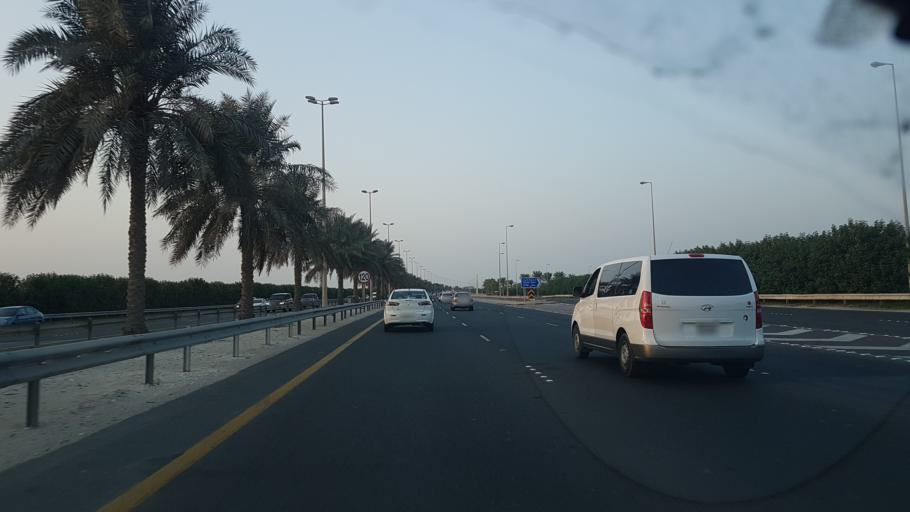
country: BH
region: Northern
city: Madinat `Isa
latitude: 26.1612
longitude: 50.5048
